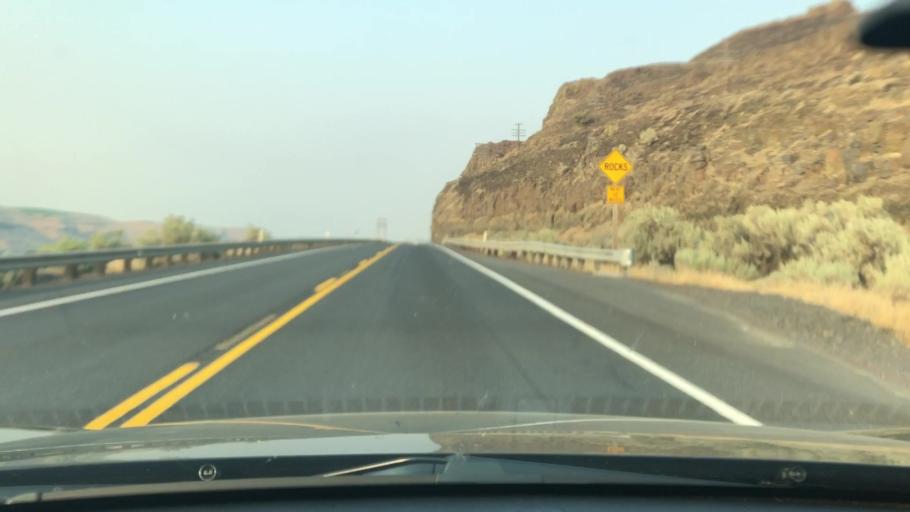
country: US
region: Washington
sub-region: Benton County
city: Highland
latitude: 45.9479
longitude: -119.0646
